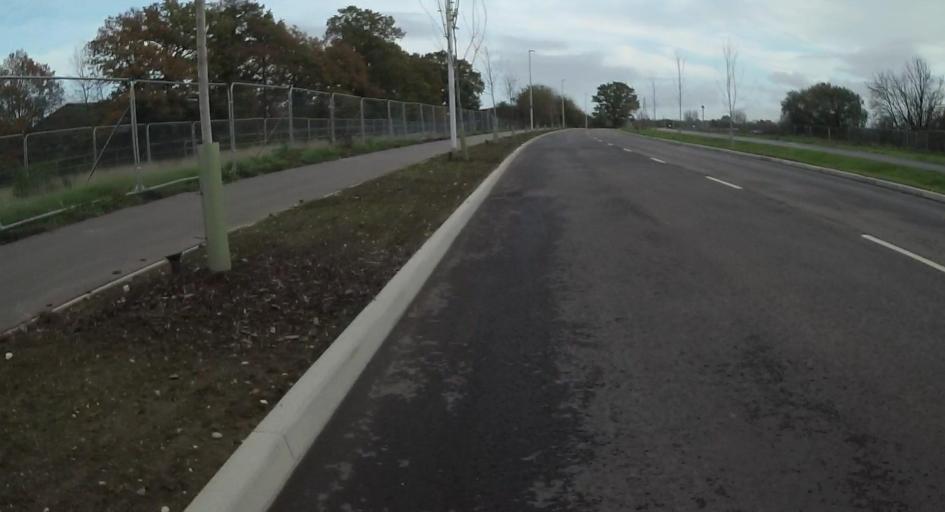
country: GB
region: England
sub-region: Hampshire
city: Eversley
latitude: 51.3759
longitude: -0.8964
